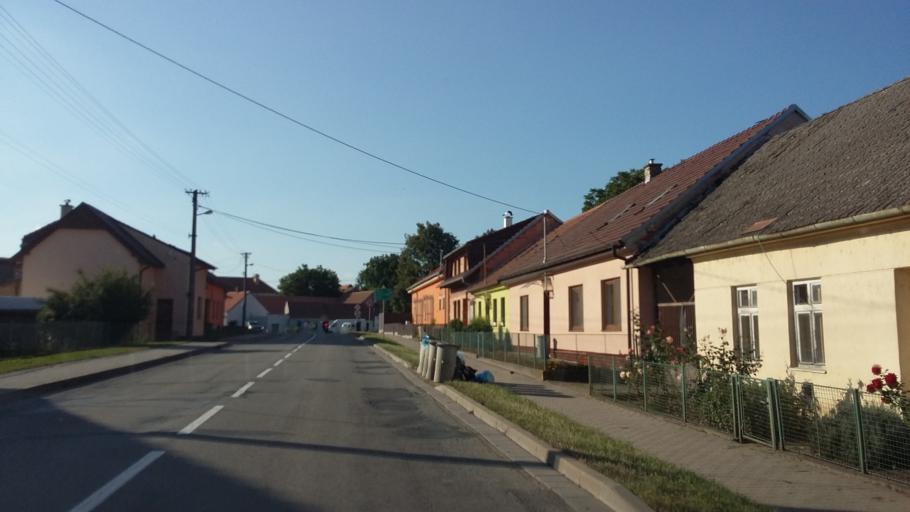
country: CZ
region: South Moravian
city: Ricany
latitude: 49.2091
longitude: 16.4127
